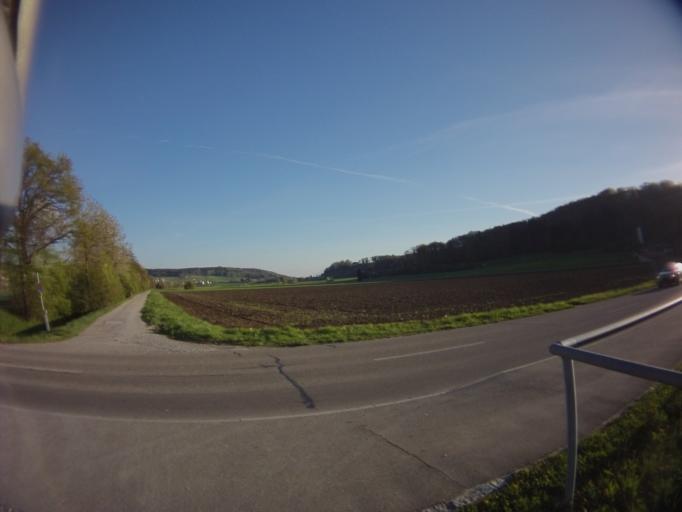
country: CH
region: Zurich
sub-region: Bezirk Affoltern
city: Wettswil / Wettswil (Dorf)
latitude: 47.3353
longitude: 8.4661
